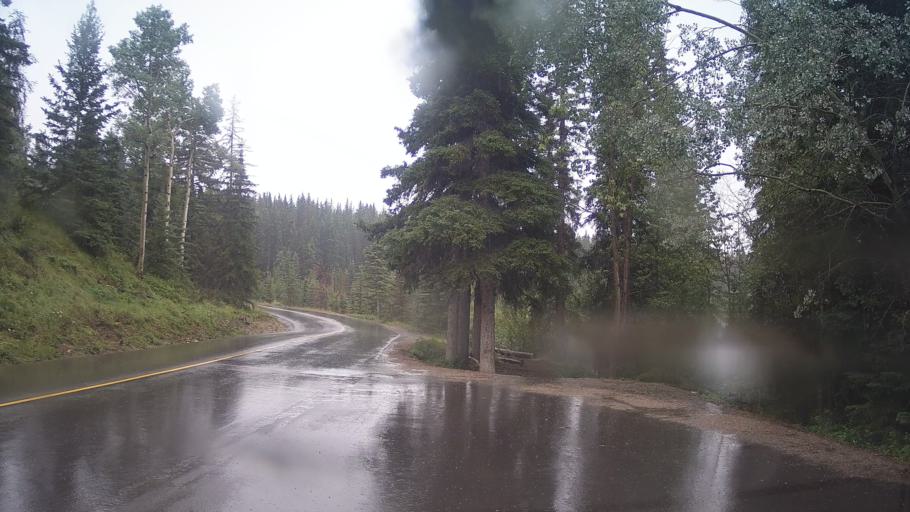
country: CA
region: Alberta
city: Jasper Park Lodge
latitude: 52.9110
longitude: -118.0925
